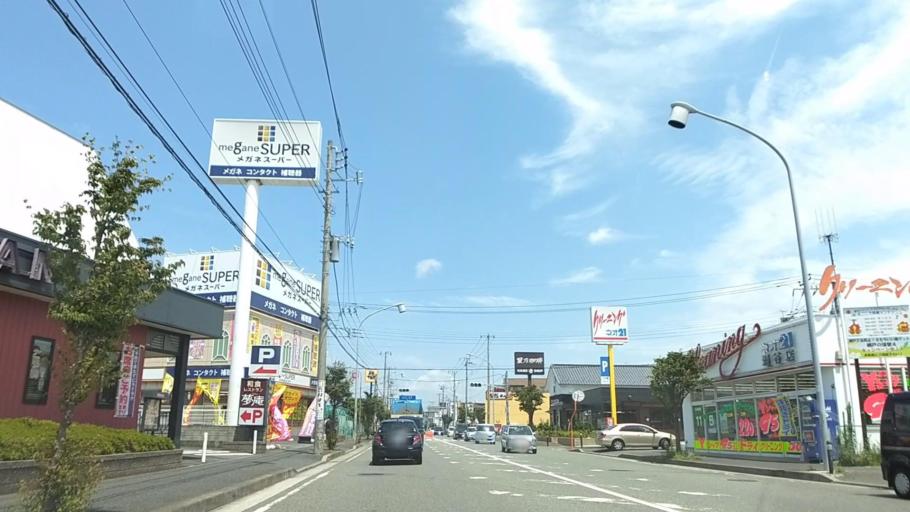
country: JP
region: Kanagawa
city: Minami-rinkan
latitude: 35.4621
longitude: 139.4802
